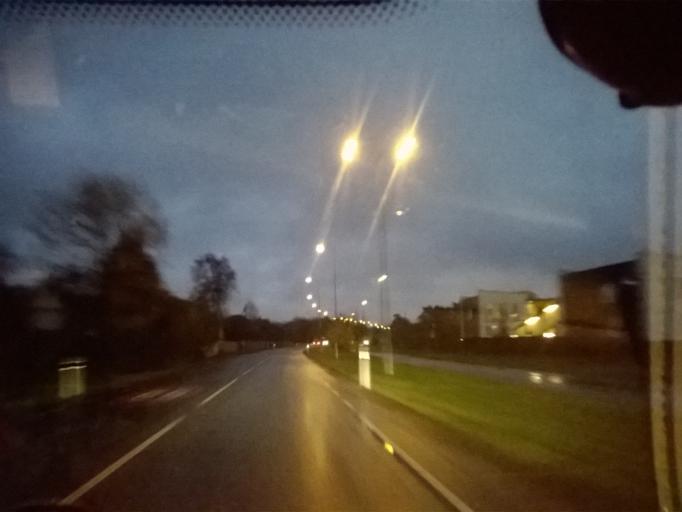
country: EE
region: Harju
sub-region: Viimsi vald
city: Viimsi
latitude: 59.5086
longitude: 24.8574
